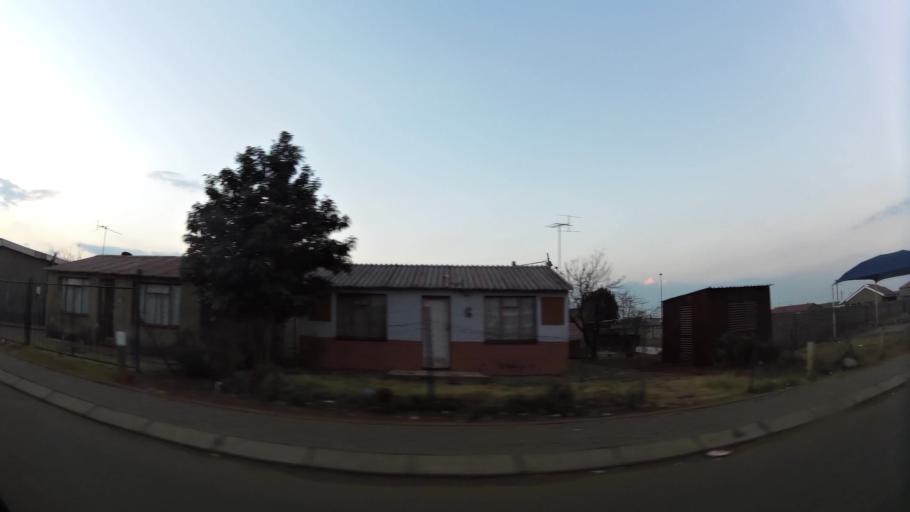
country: ZA
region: Gauteng
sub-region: City of Johannesburg Metropolitan Municipality
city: Orange Farm
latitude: -26.5582
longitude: 27.8662
